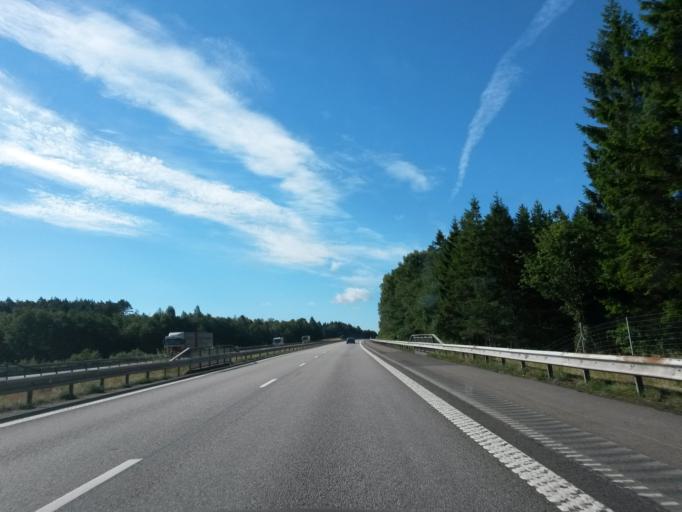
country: SE
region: Halland
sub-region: Kungsbacka Kommun
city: Frillesas
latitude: 57.3598
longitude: 12.2082
